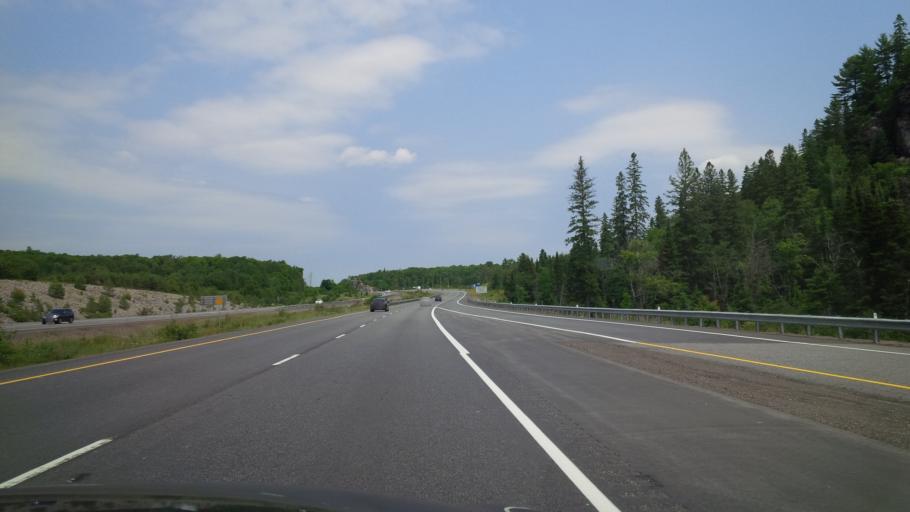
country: CA
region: Ontario
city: Huntsville
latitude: 45.4144
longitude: -79.2390
